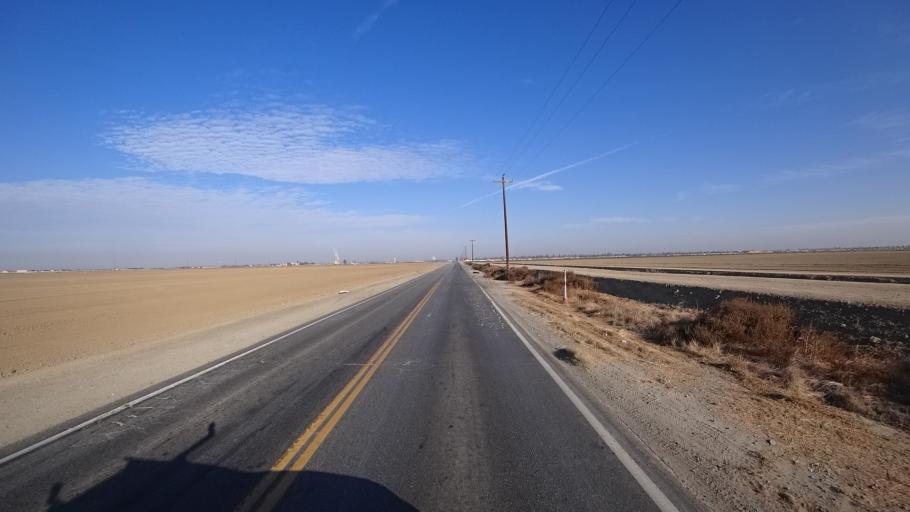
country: US
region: California
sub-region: Kern County
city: Greenfield
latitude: 35.2822
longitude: -119.0922
